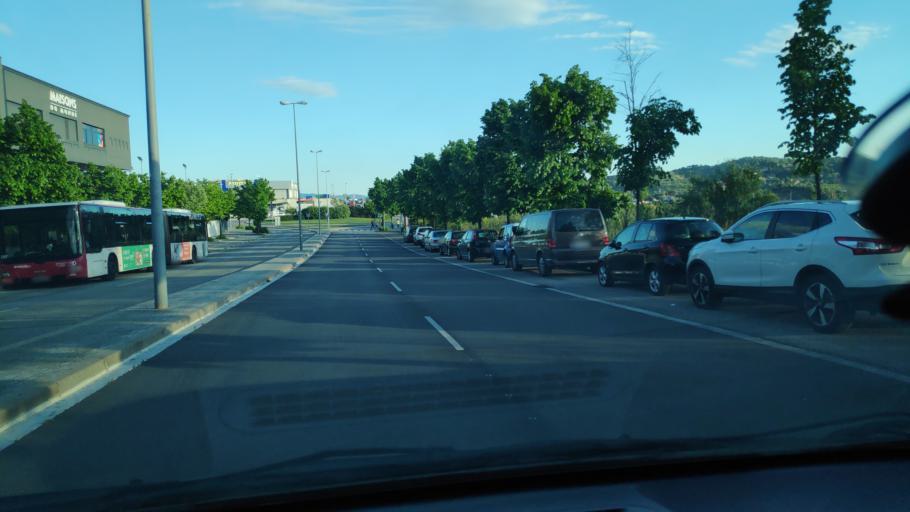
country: ES
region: Catalonia
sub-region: Provincia de Barcelona
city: Terrassa
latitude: 41.5464
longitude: 2.0238
